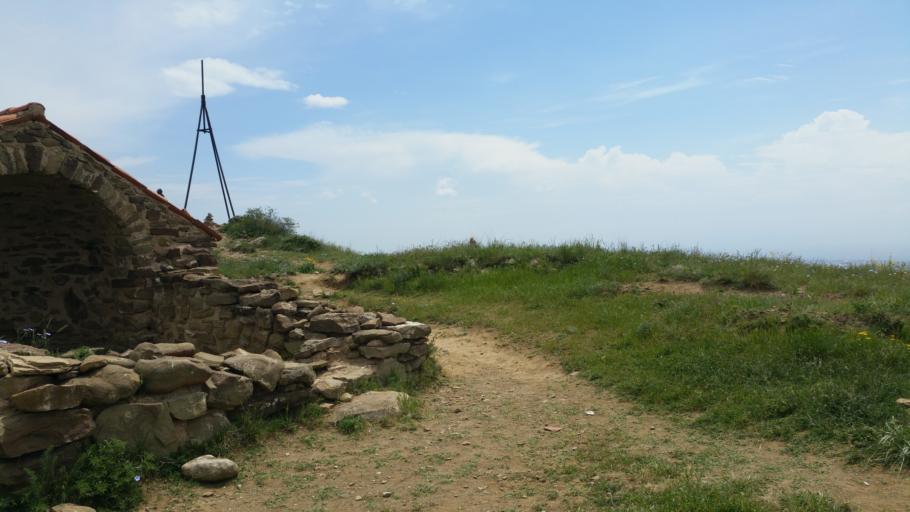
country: AZ
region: Agstafa
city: Saloglu
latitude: 41.4410
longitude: 45.3775
